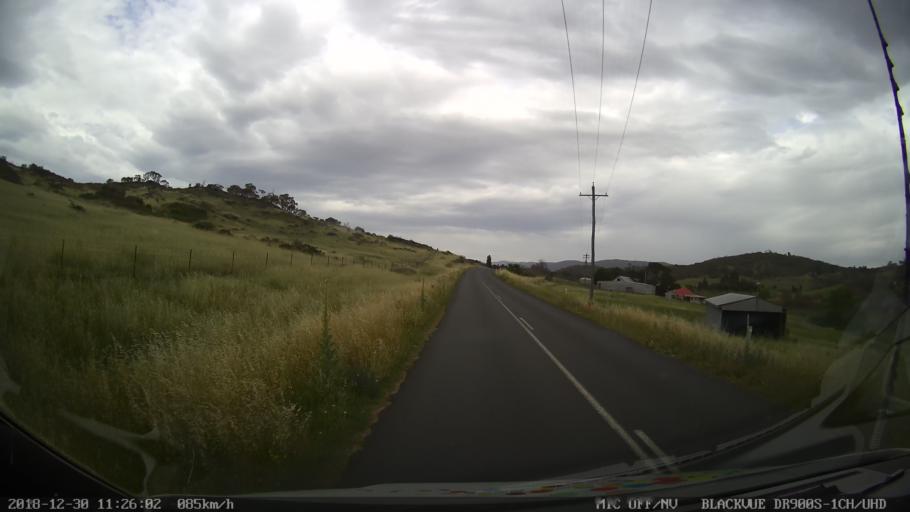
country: AU
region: New South Wales
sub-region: Snowy River
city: Jindabyne
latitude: -36.4686
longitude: 148.6396
